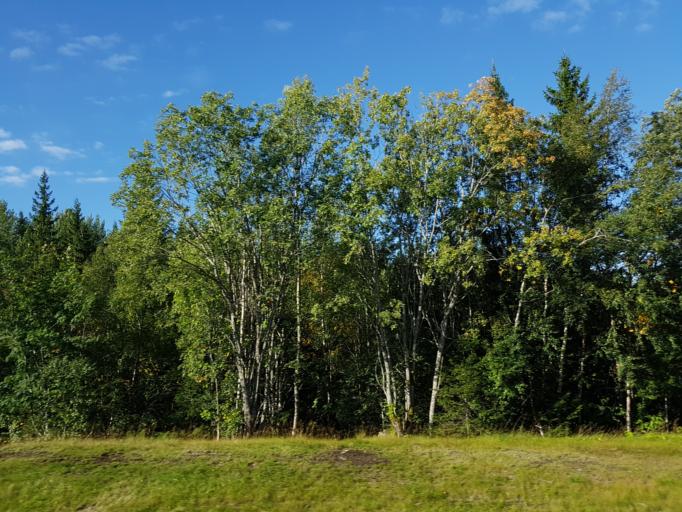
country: NO
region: Sor-Trondelag
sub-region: Trondheim
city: Trondheim
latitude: 63.6418
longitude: 10.2696
